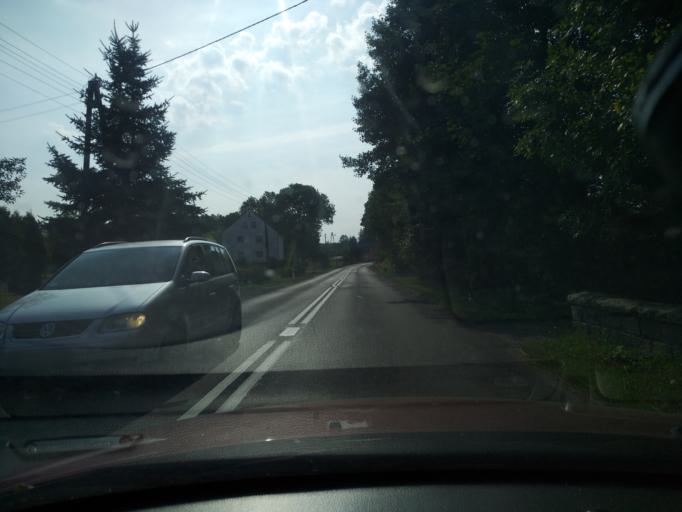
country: PL
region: Lower Silesian Voivodeship
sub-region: Powiat lwowecki
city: Lubomierz
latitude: 50.9726
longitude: 15.5022
